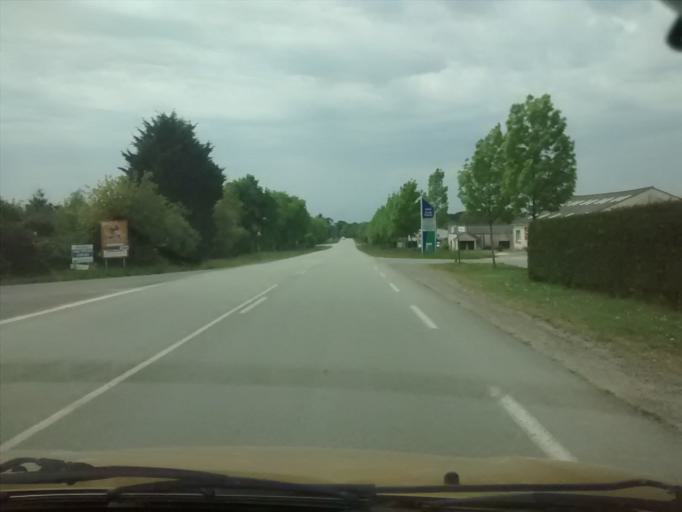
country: FR
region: Brittany
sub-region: Departement du Morbihan
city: Berric
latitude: 47.6282
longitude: -2.5314
